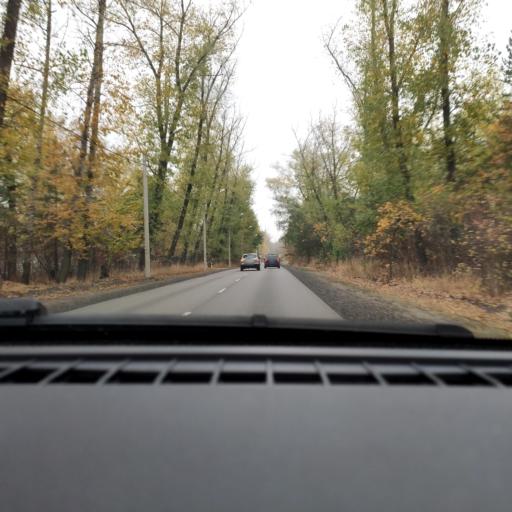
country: RU
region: Voronezj
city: Somovo
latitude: 51.7174
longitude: 39.3231
